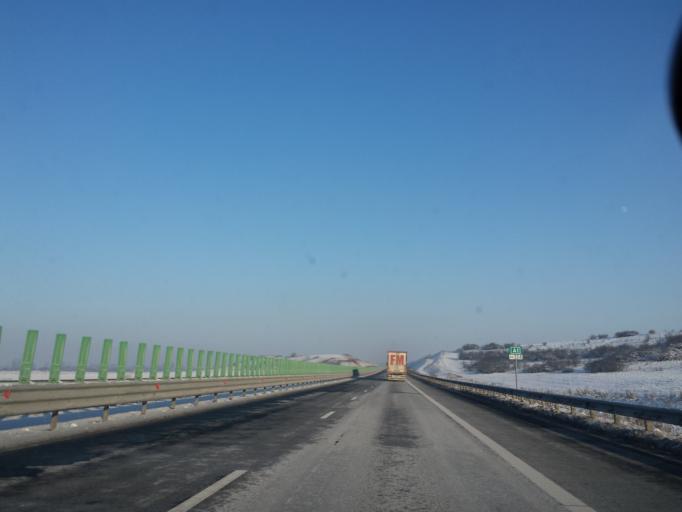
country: RO
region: Alba
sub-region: Comuna Saliste
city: Salistea
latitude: 45.9352
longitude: 23.3827
